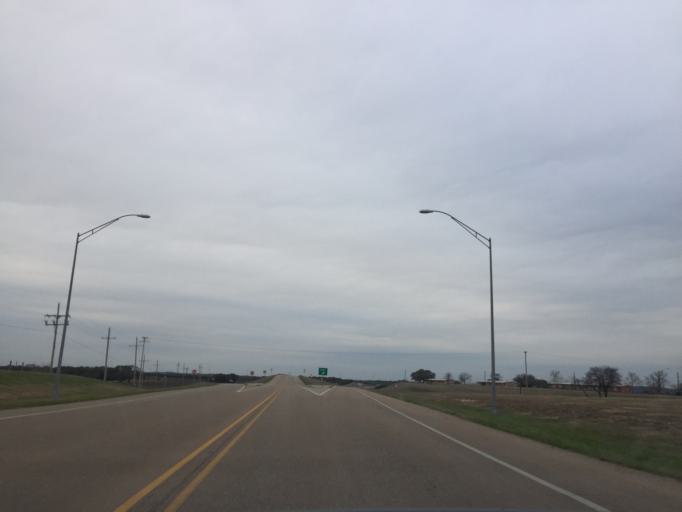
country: US
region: Texas
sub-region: Coryell County
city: Gatesville
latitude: 31.4808
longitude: -97.7295
